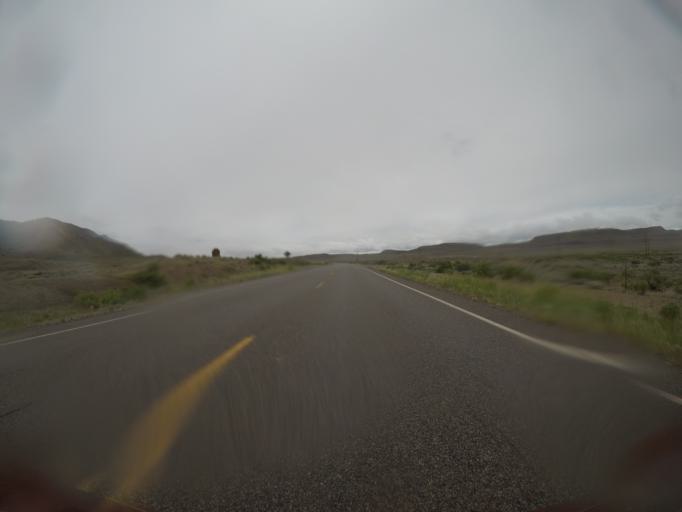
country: US
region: Wyoming
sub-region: Big Horn County
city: Lovell
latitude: 44.9518
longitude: -108.2957
